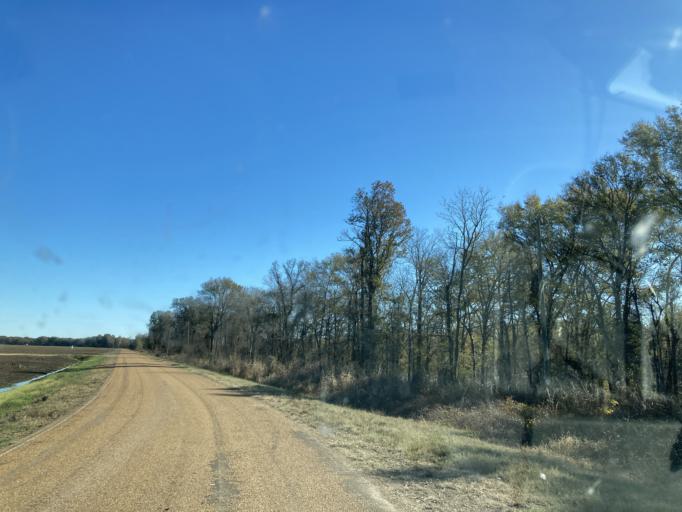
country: US
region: Mississippi
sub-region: Yazoo County
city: Yazoo City
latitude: 32.7399
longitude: -90.6362
